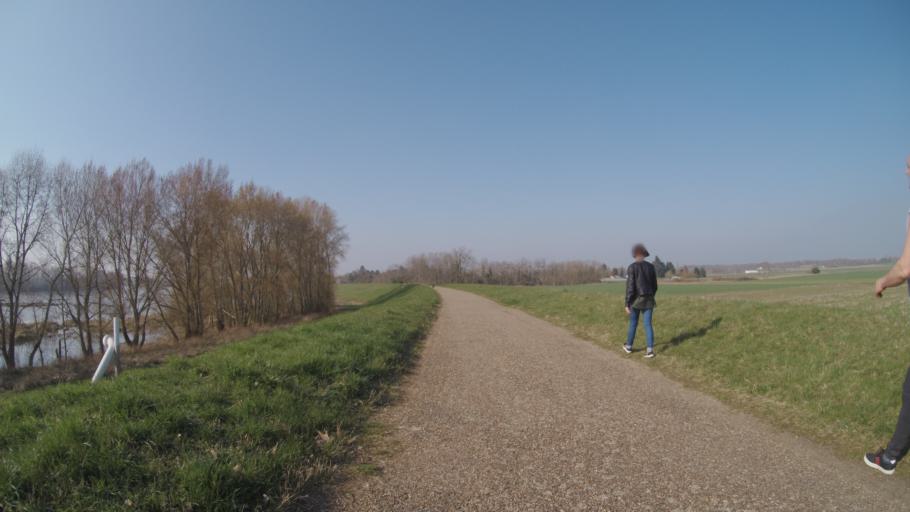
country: FR
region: Centre
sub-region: Departement du Loiret
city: Checy
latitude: 47.8777
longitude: 2.0357
